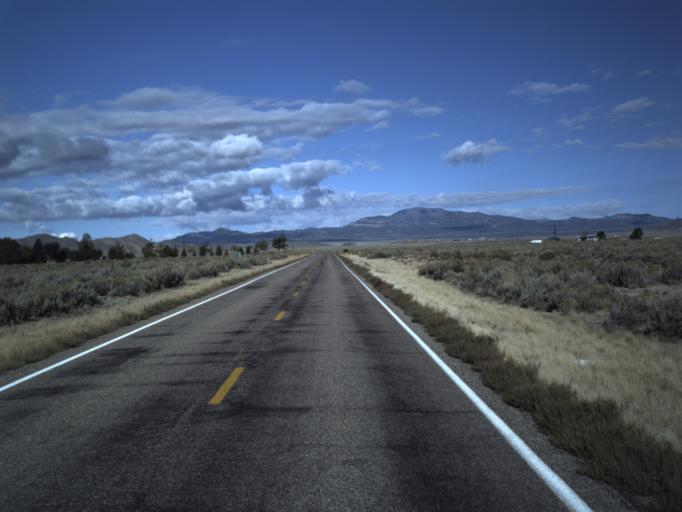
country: US
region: Utah
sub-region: Beaver County
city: Milford
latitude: 38.4038
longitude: -113.0432
